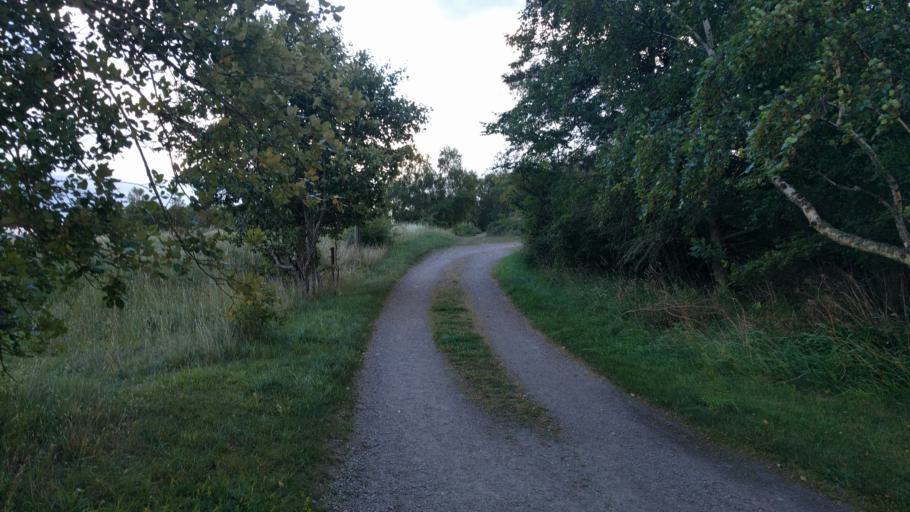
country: SE
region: Skane
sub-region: Angelholms Kommun
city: Vejbystrand
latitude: 56.2314
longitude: 12.7229
